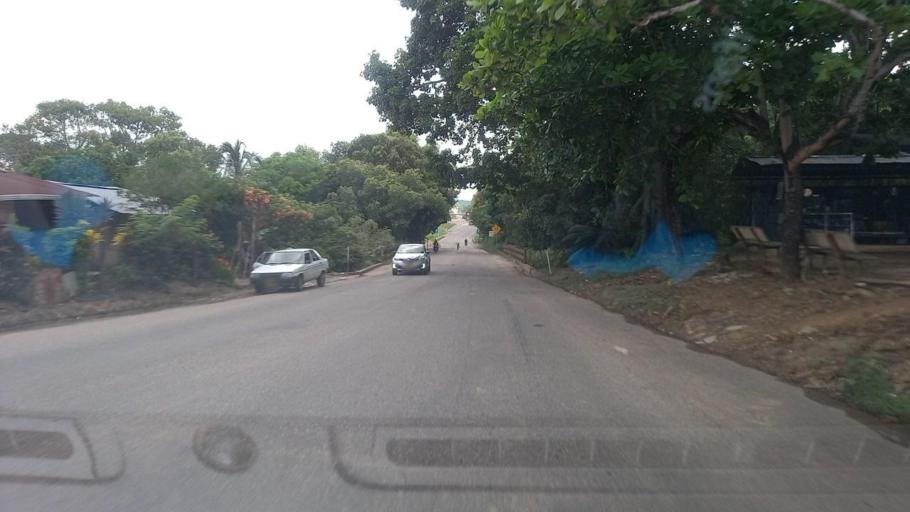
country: CO
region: Santander
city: Sabana de Torres
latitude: 7.1313
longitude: -73.5607
